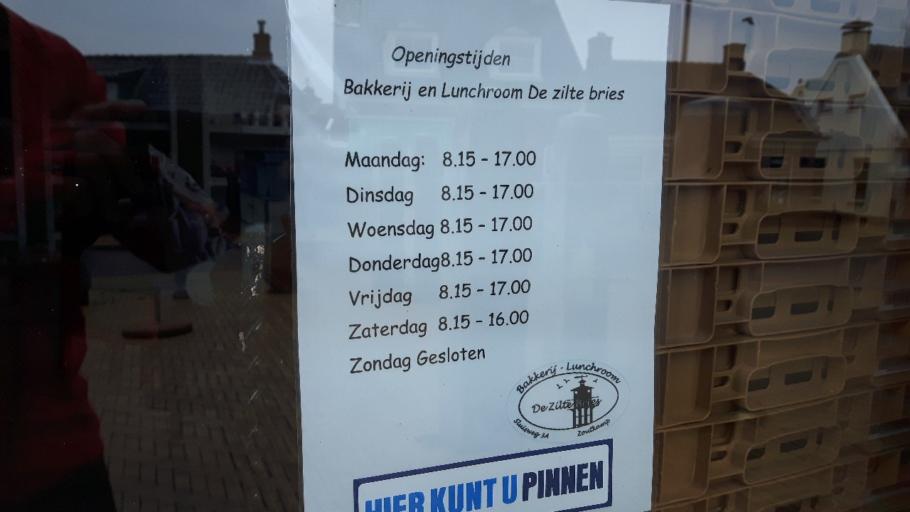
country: NL
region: Groningen
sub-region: Gemeente De Marne
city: Ulrum
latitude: 53.3374
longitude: 6.3007
